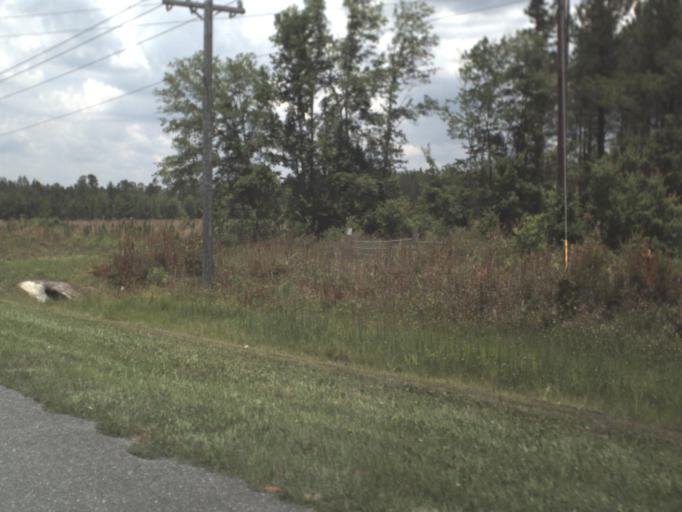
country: US
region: Florida
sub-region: Columbia County
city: Watertown
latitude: 30.1623
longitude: -82.5692
